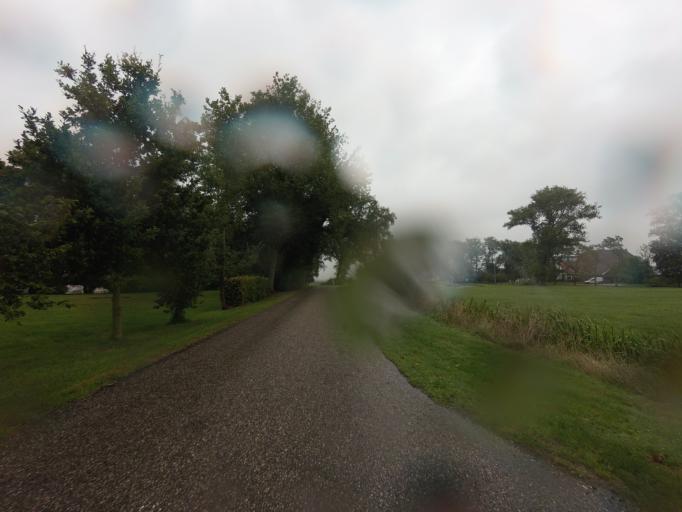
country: NL
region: Friesland
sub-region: Gemeente Boarnsterhim
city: Aldeboarn
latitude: 53.0632
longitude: 5.9169
